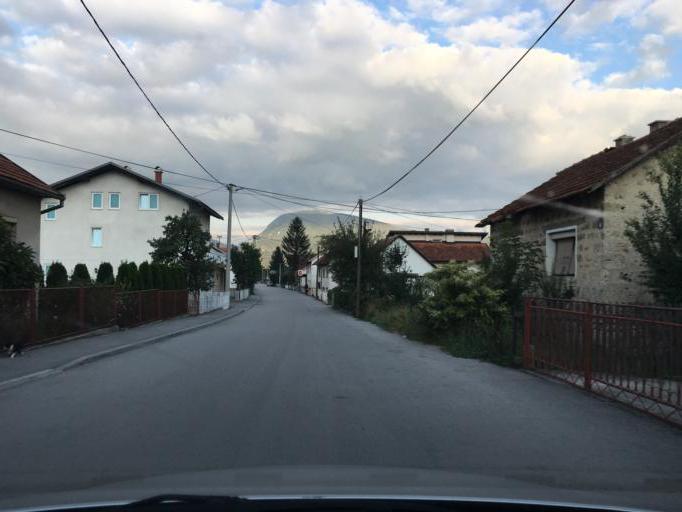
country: BA
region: Federation of Bosnia and Herzegovina
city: Bugojno
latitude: 44.0605
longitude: 17.4509
